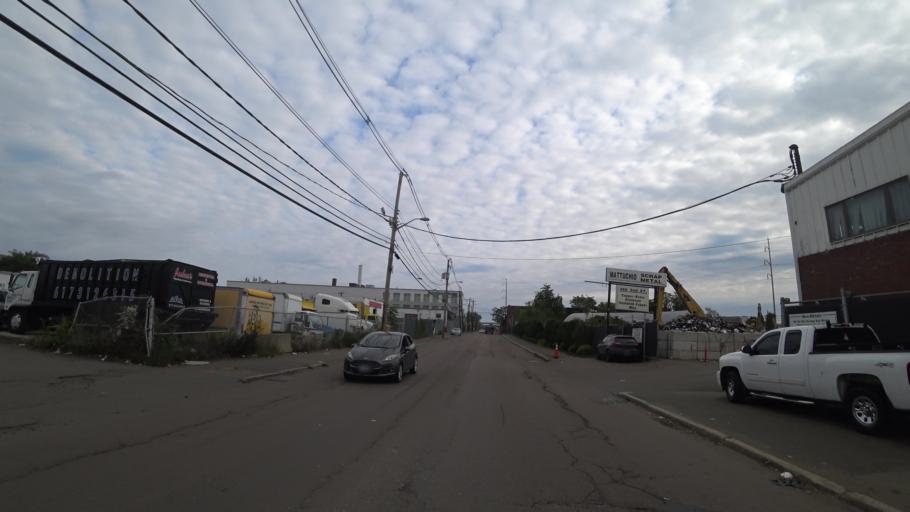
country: US
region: Massachusetts
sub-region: Middlesex County
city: Everett
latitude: 42.3998
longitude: -71.0496
